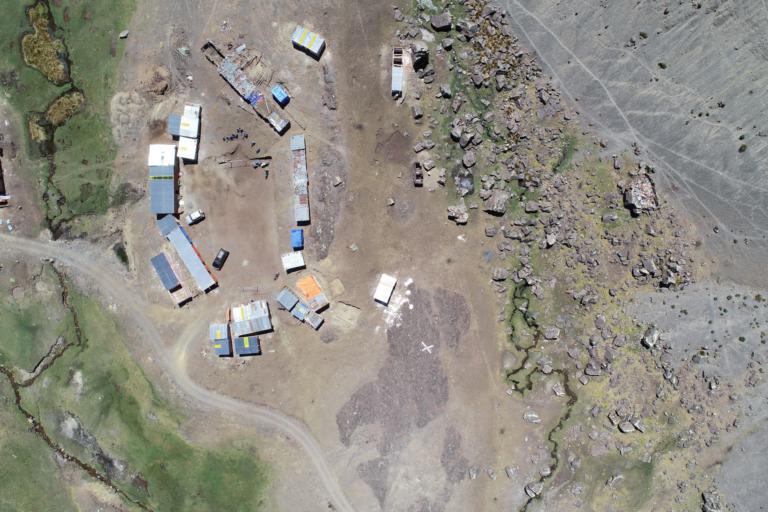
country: BO
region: La Paz
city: La Paz
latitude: -16.6216
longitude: -67.8282
